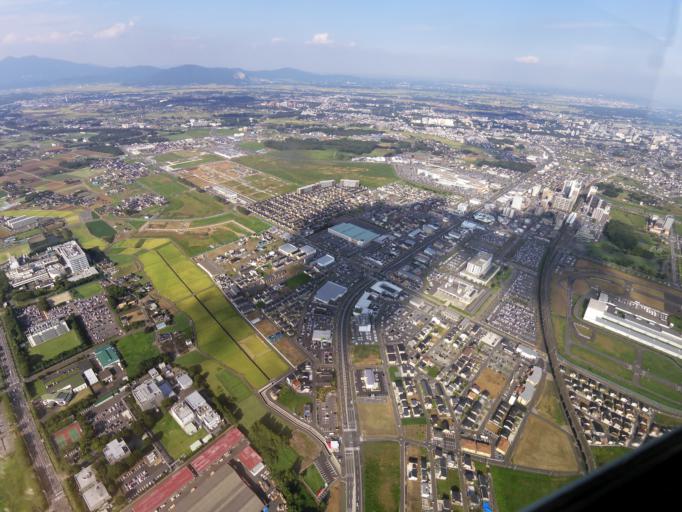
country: JP
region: Ibaraki
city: Naka
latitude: 36.0822
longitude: 140.0678
